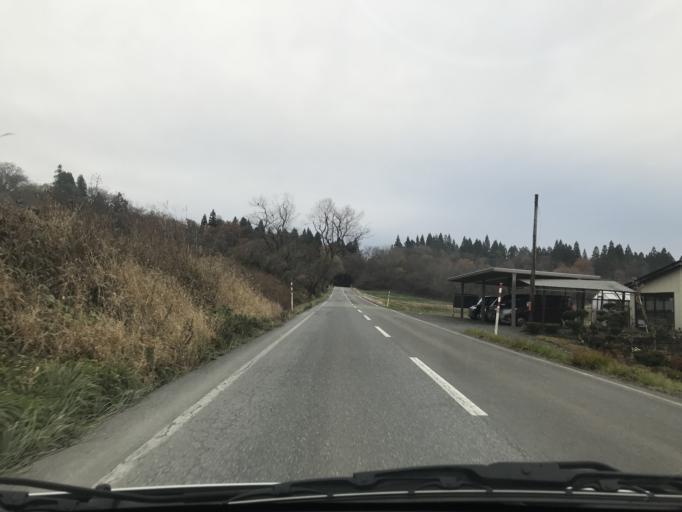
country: JP
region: Iwate
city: Kitakami
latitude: 39.2538
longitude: 141.2677
